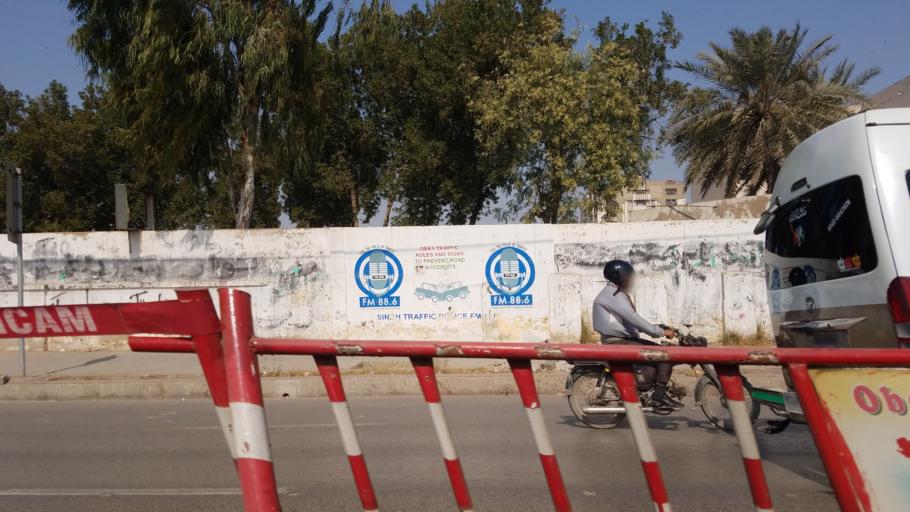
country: PK
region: Sindh
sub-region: Karachi District
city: Karachi
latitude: 24.8502
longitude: 67.0122
